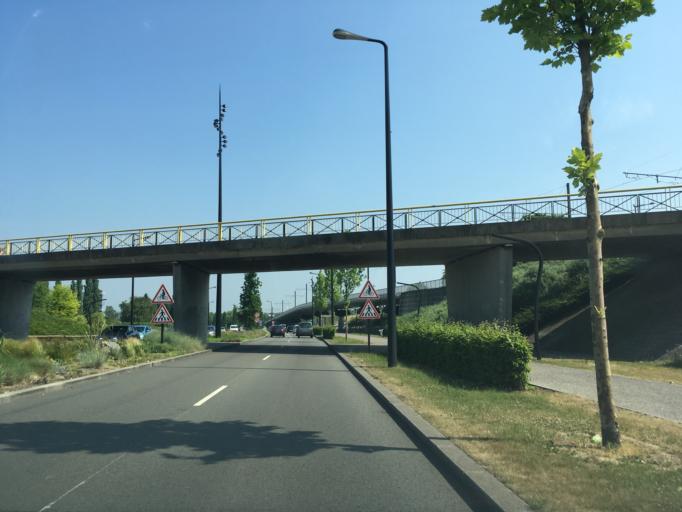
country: FR
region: Nord-Pas-de-Calais
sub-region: Departement du Nord
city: Valenciennes
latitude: 50.3423
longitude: 3.5155
